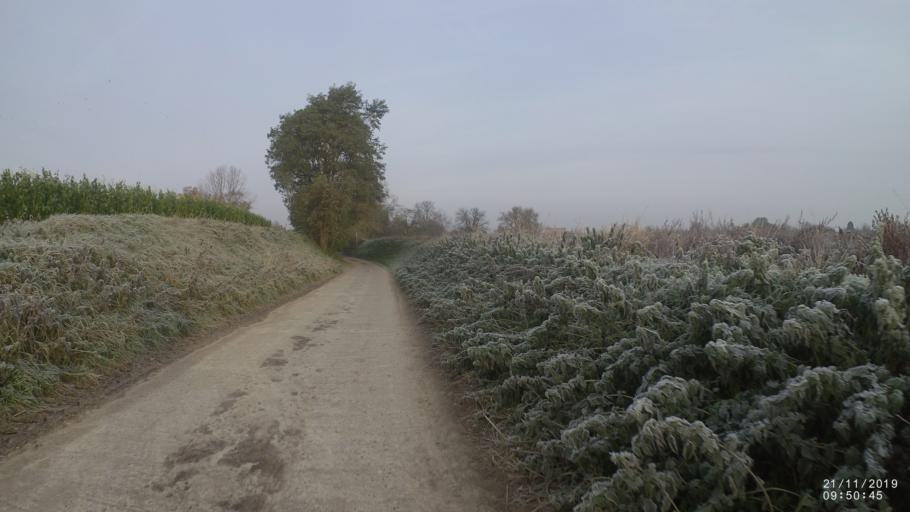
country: BE
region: Flanders
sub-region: Provincie Vlaams-Brabant
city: Landen
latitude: 50.7962
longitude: 5.0164
